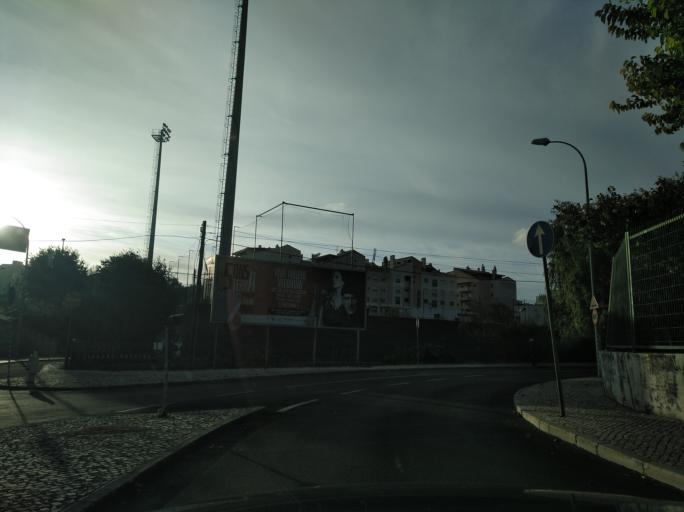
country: PT
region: Lisbon
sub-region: Oeiras
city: Linda-a-Velha
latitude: 38.7224
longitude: -9.2251
